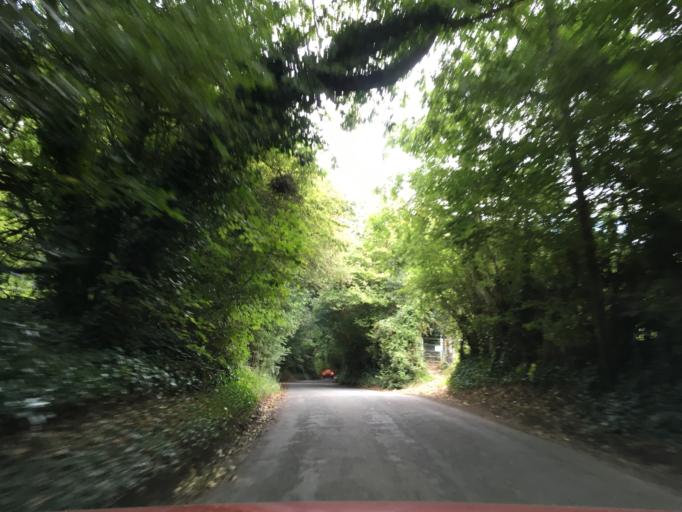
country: GB
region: England
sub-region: South Gloucestershire
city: Alveston
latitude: 51.5813
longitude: -2.5379
